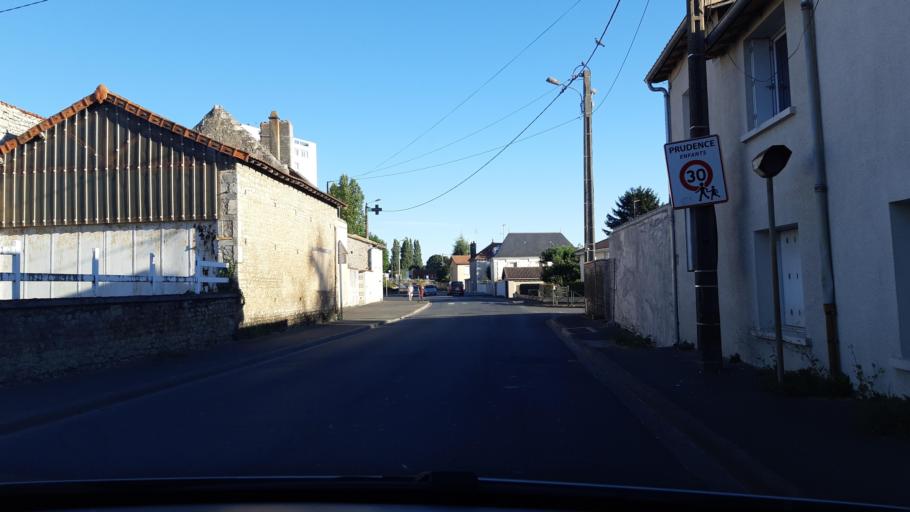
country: FR
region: Poitou-Charentes
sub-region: Departement des Deux-Sevres
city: Exireuil
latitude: 46.4168
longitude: -0.2025
